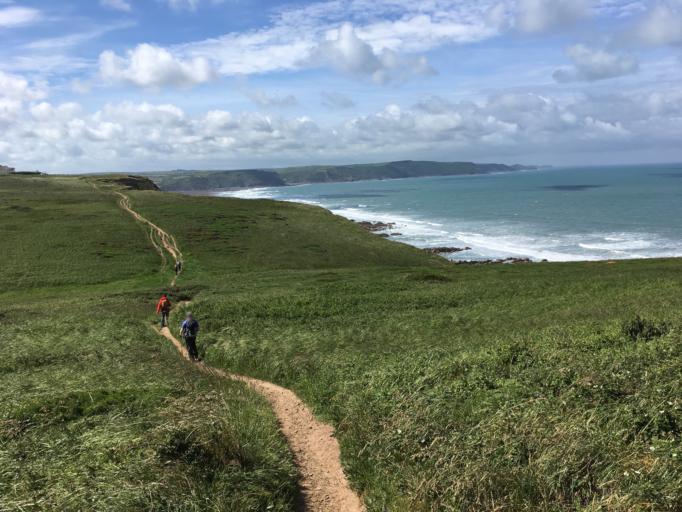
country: GB
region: England
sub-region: Cornwall
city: Bude
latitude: 50.8064
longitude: -4.5573
